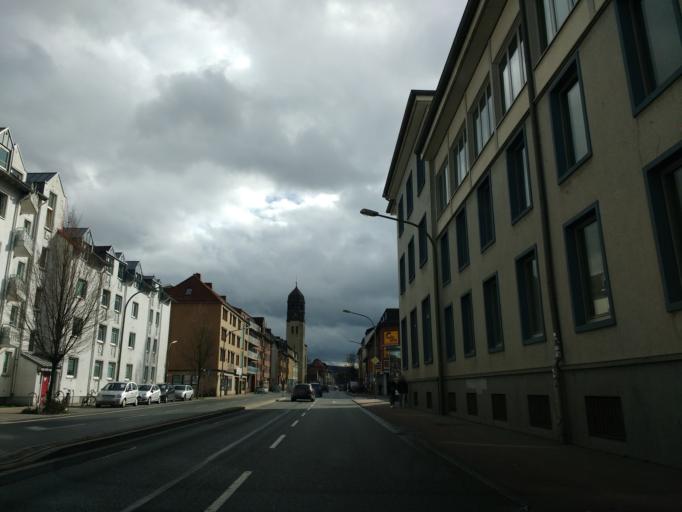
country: DE
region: Lower Saxony
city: Osnabrueck
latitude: 52.2626
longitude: 8.0555
